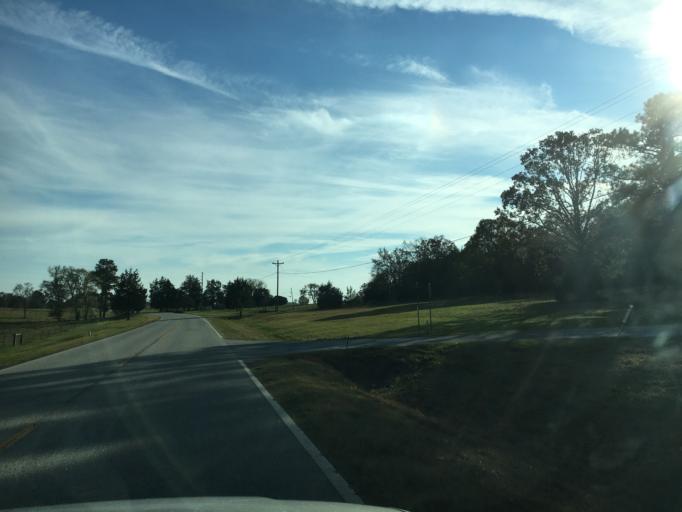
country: US
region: Georgia
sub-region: Elbert County
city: Elberton
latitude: 34.0033
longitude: -82.7808
